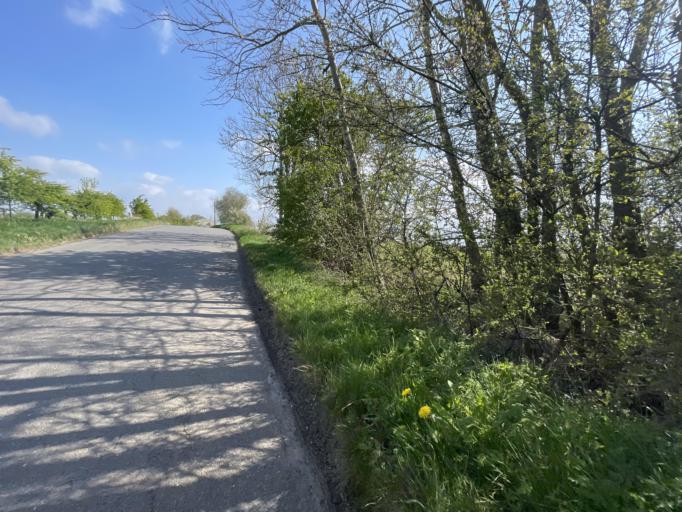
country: GB
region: England
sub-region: Warwickshire
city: Rugby
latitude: 52.3440
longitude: -1.2379
